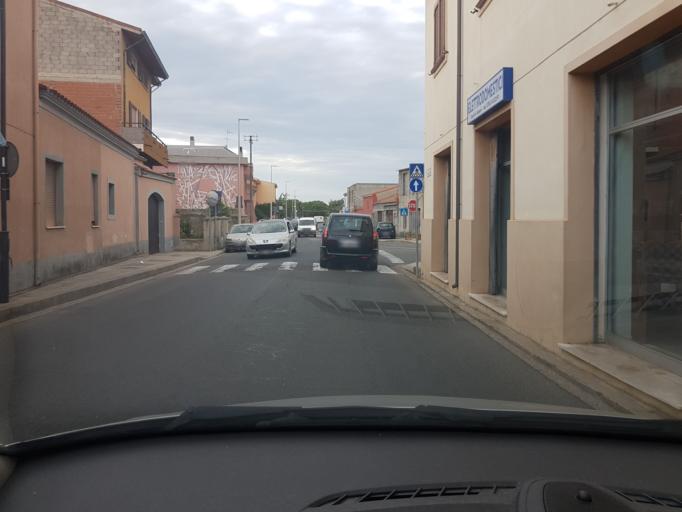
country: IT
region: Sardinia
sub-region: Provincia di Oristano
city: Riola Sardo
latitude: 39.9962
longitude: 8.5390
